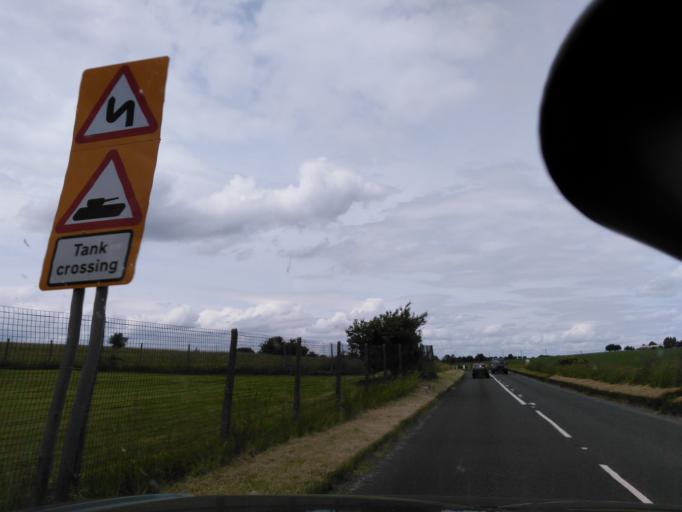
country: GB
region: England
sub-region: Wiltshire
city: Shrewton
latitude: 51.2205
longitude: -1.9443
